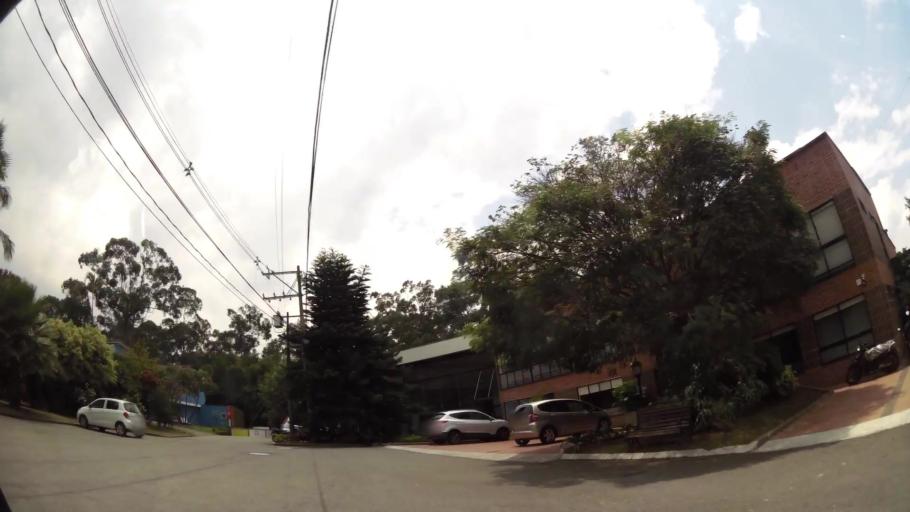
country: CO
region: Antioquia
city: Envigado
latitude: 6.1865
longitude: -75.5752
